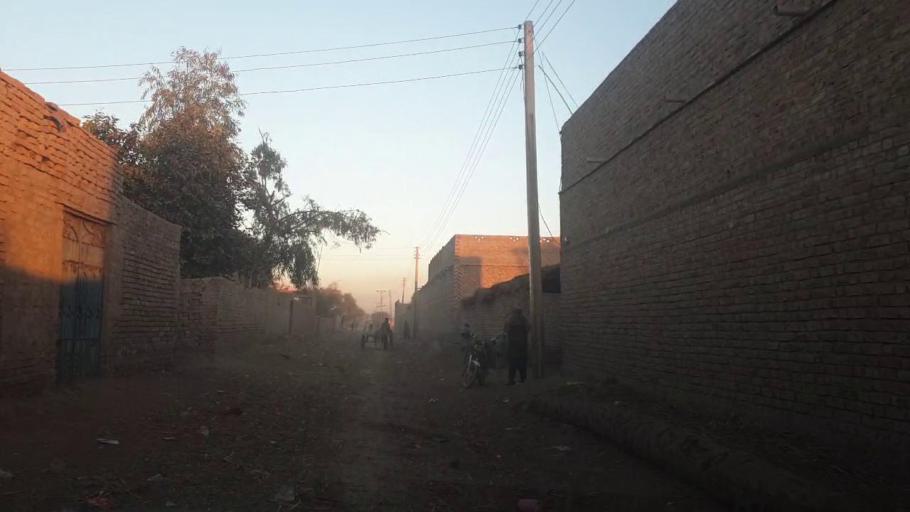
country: PK
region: Sindh
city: Ghotki
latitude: 28.0387
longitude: 69.3118
